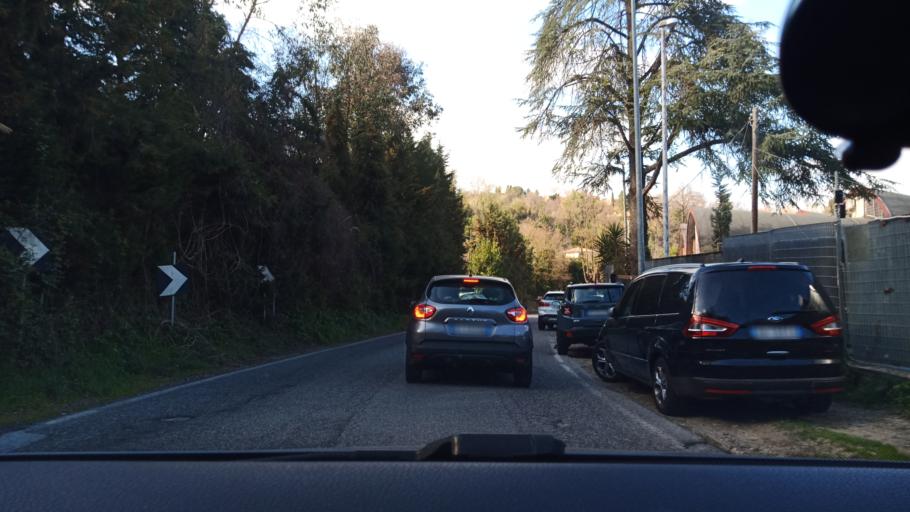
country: IT
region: Latium
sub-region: Citta metropolitana di Roma Capitale
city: Torrita Tiberina
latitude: 42.2398
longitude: 12.6172
